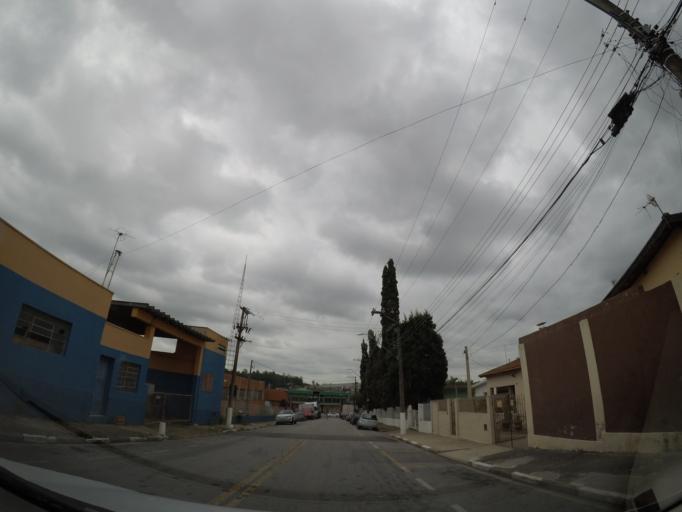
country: BR
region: Sao Paulo
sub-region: Louveira
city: Louveira
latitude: -23.0858
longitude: -46.9782
